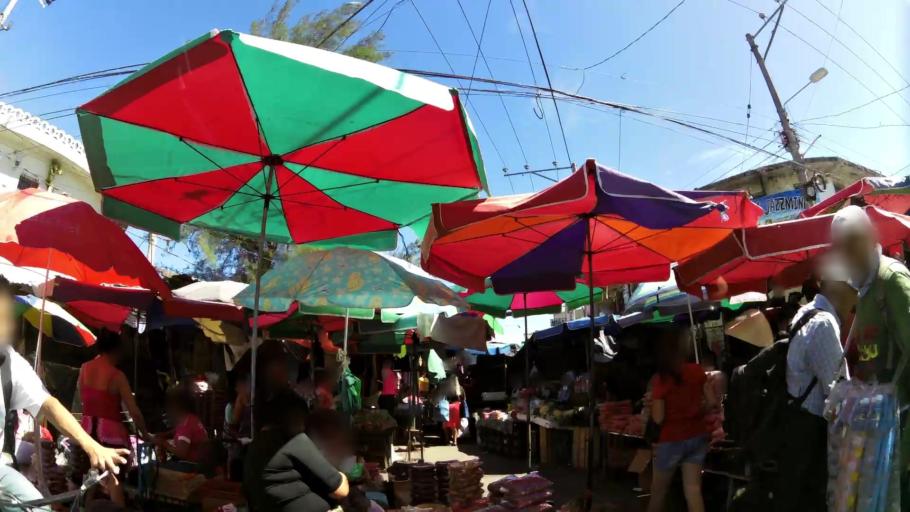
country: SV
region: San Salvador
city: Apopa
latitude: 13.8005
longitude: -89.1788
